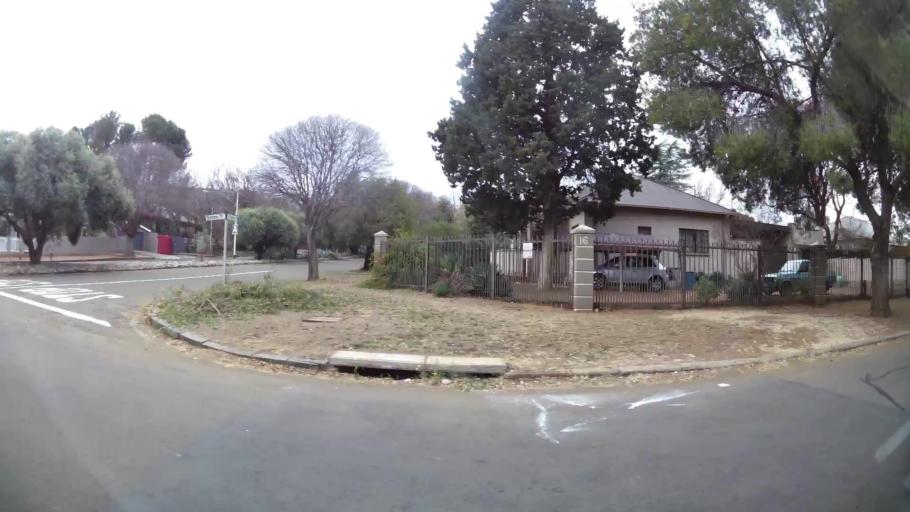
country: ZA
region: Orange Free State
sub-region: Mangaung Metropolitan Municipality
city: Bloemfontein
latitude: -29.1013
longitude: 26.2104
